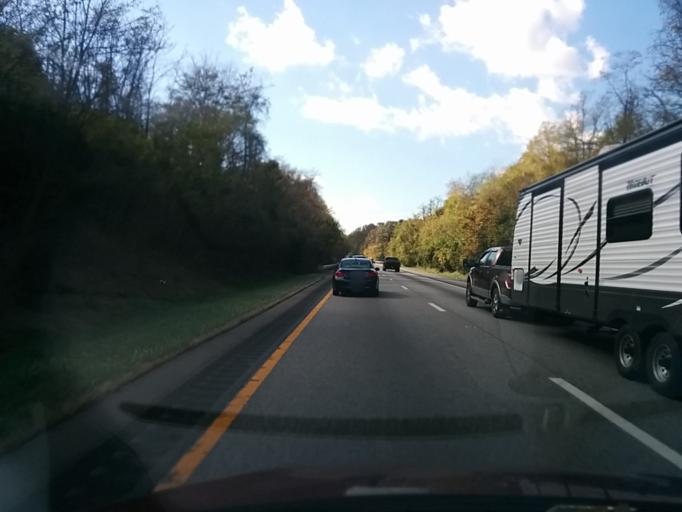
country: US
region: Virginia
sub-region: Botetourt County
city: Daleville
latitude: 37.4370
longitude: -79.8697
